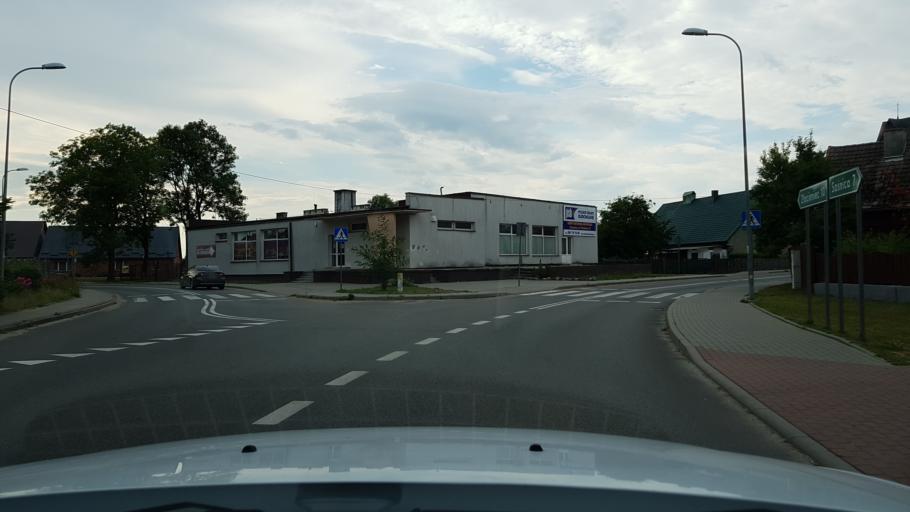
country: PL
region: West Pomeranian Voivodeship
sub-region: Powiat drawski
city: Wierzchowo
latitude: 53.4595
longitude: 16.1022
